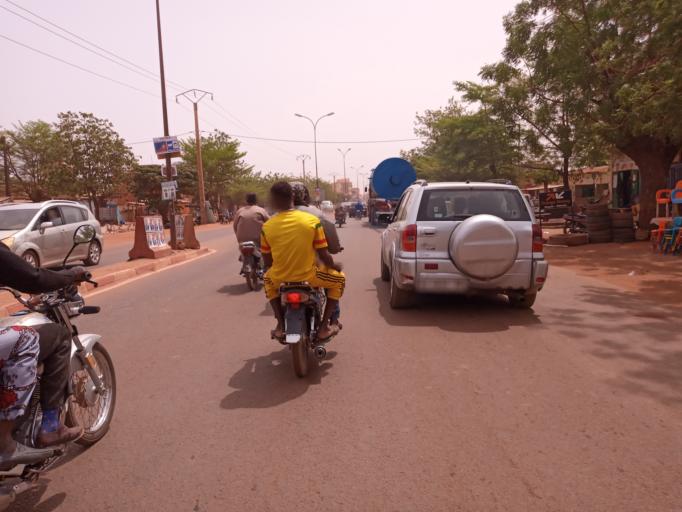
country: ML
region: Bamako
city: Bamako
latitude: 12.6702
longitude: -7.9200
